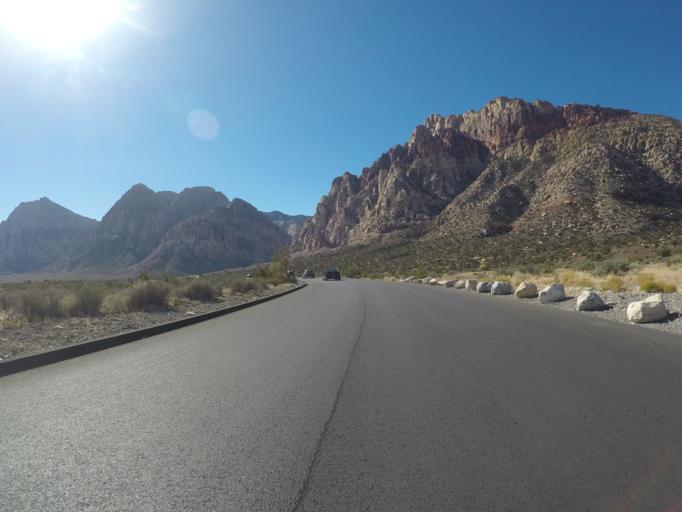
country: US
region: Nevada
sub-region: Clark County
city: Summerlin South
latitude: 36.1388
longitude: -115.4732
